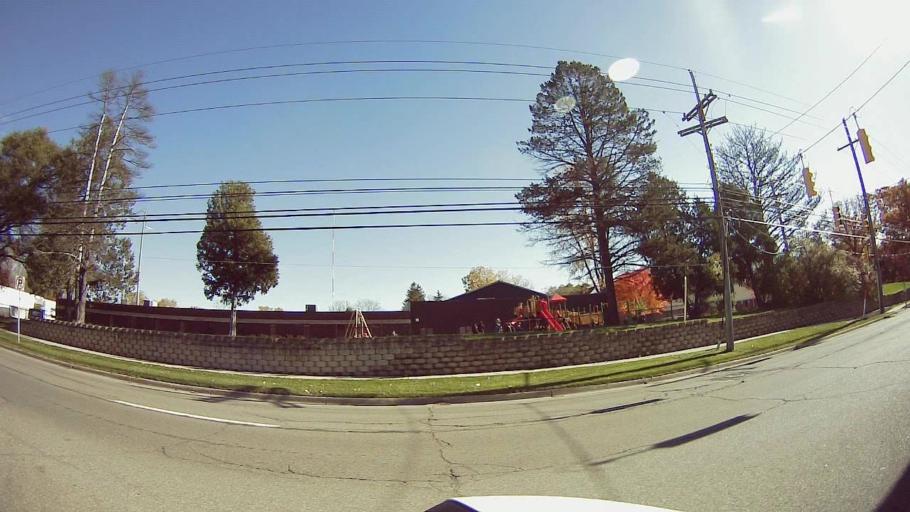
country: US
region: Michigan
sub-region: Oakland County
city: Southfield
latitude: 42.4691
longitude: -83.2607
